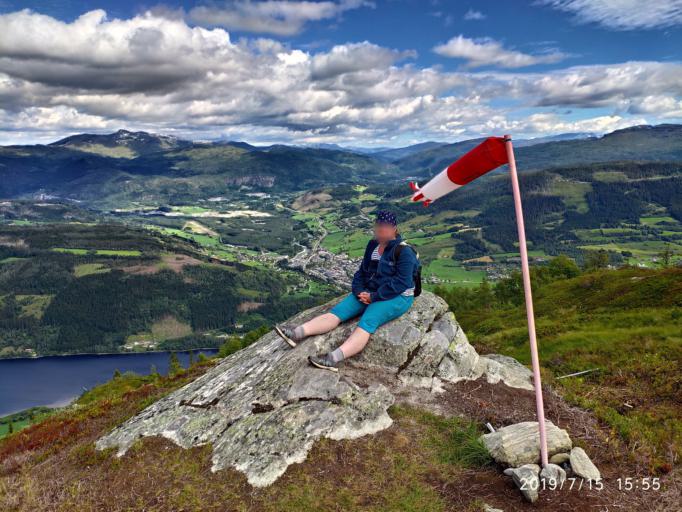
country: NO
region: Hordaland
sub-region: Voss
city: Voss
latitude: 60.6457
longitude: 6.4078
